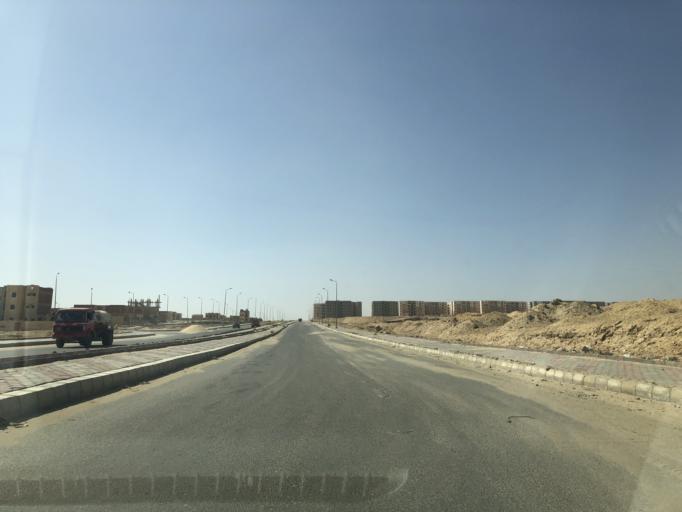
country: EG
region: Al Jizah
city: Madinat Sittah Uktubar
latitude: 29.9306
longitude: 31.0125
